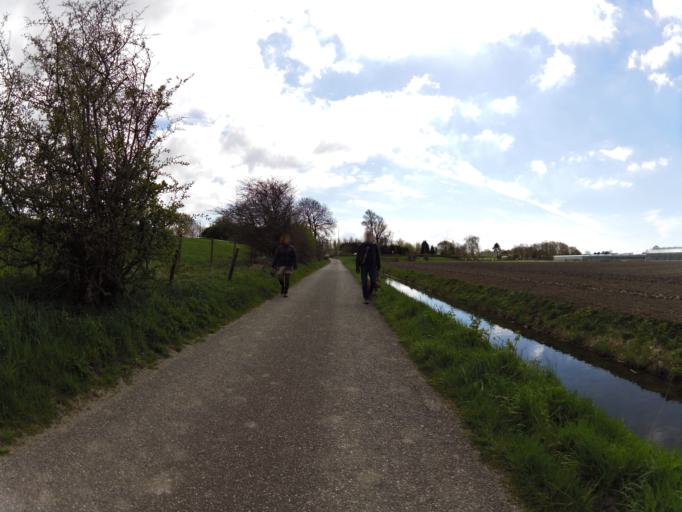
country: NL
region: South Holland
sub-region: Gemeente Hellevoetsluis
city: Nieuw-Helvoet
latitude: 51.8853
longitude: 4.0782
